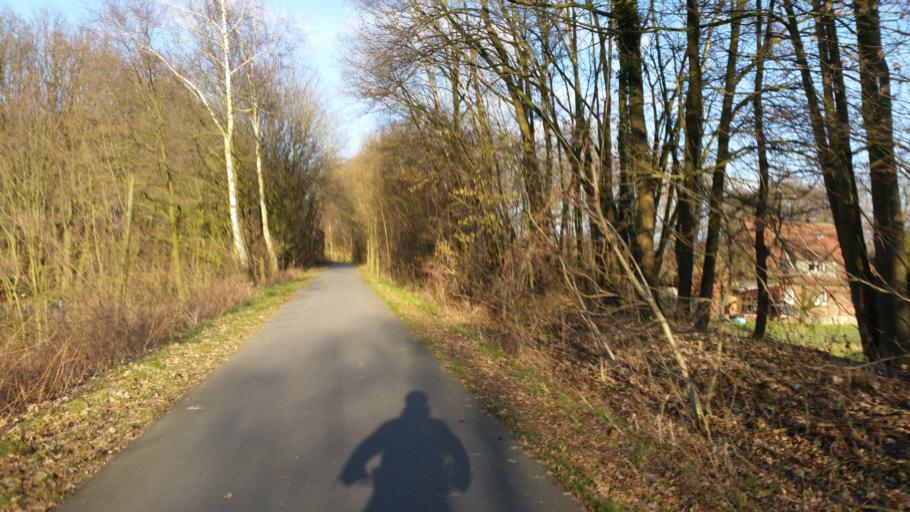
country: DE
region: North Rhine-Westphalia
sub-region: Regierungsbezirk Munster
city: Wettringen
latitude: 52.2230
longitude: 7.3432
